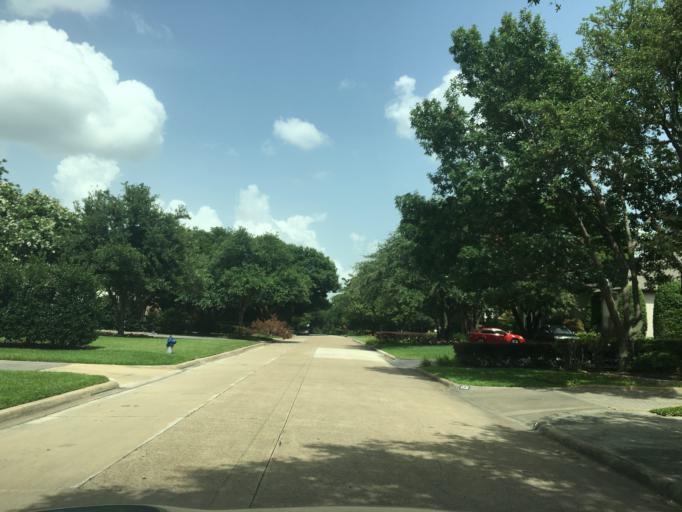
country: US
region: Texas
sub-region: Dallas County
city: University Park
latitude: 32.8873
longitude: -96.7918
